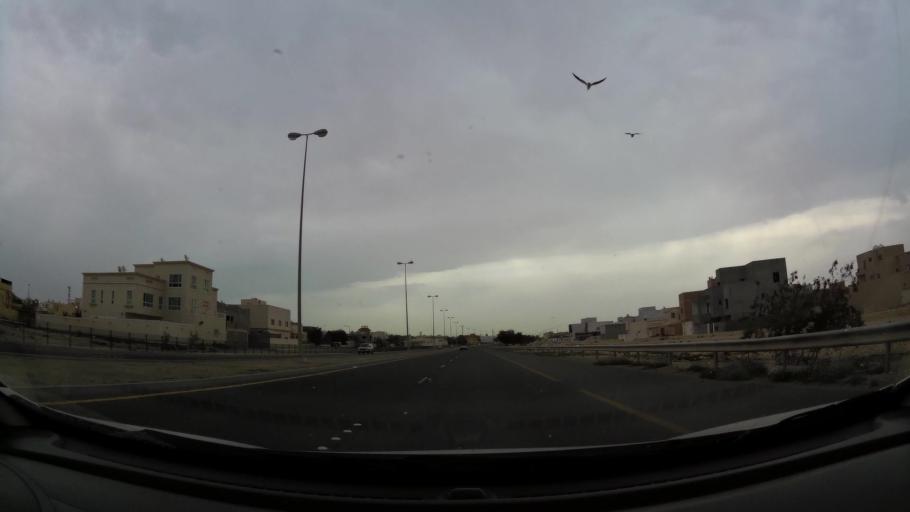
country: BH
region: Central Governorate
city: Madinat Hamad
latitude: 26.1091
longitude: 50.4958
